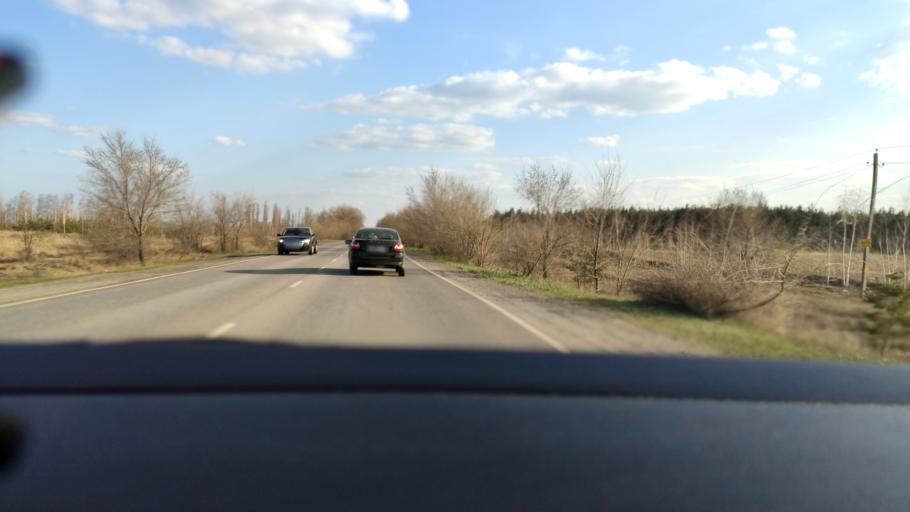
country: RU
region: Voronezj
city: Maslovka
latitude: 51.5647
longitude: 39.2736
